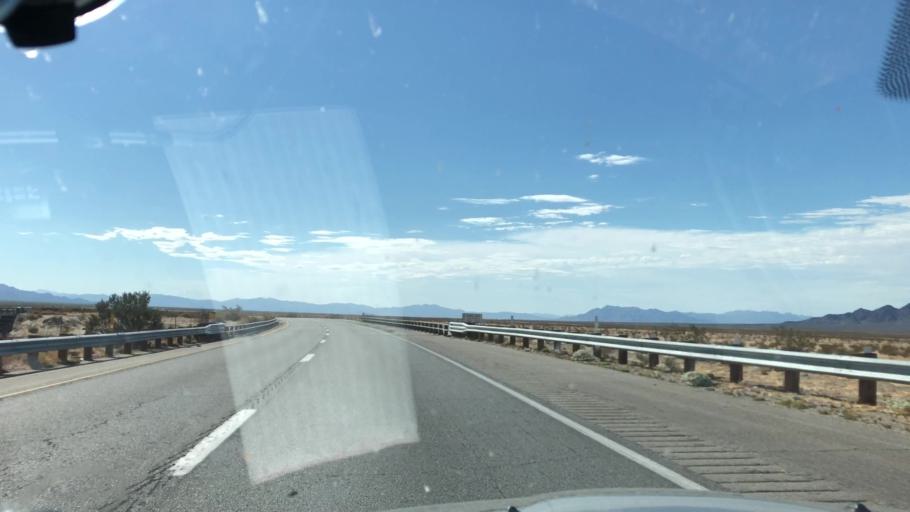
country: US
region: California
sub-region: Riverside County
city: Mesa Verde
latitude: 33.6357
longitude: -115.0812
